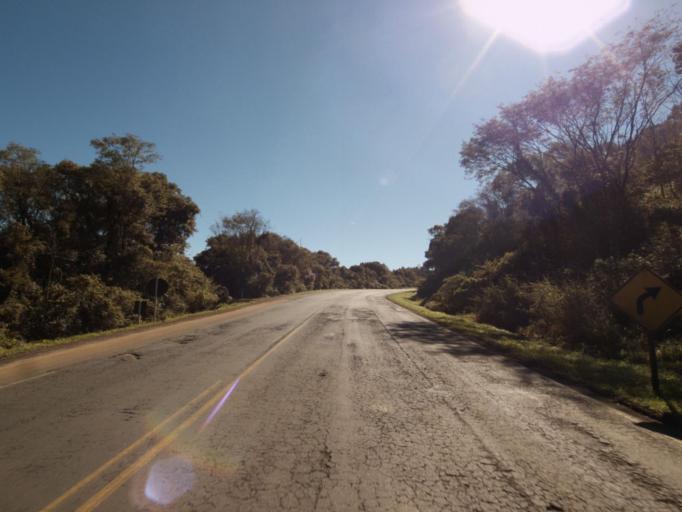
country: BR
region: Rio Grande do Sul
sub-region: Frederico Westphalen
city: Frederico Westphalen
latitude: -26.8444
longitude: -53.1709
